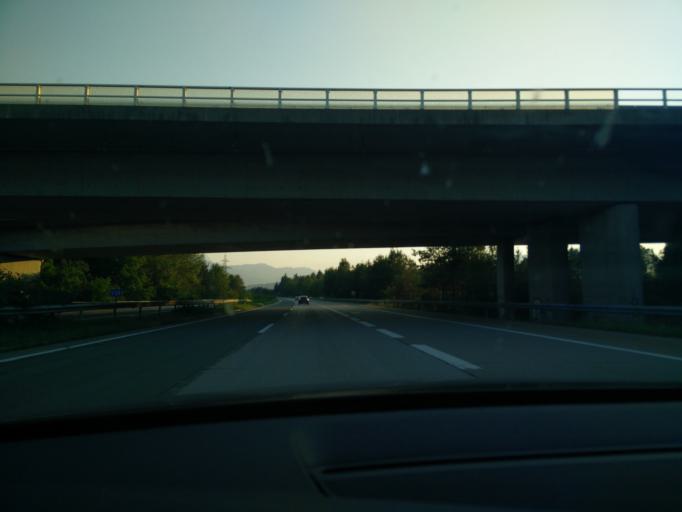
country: AT
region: Carinthia
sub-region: Politischer Bezirk Villach Land
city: Wernberg
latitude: 46.6186
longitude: 13.9049
